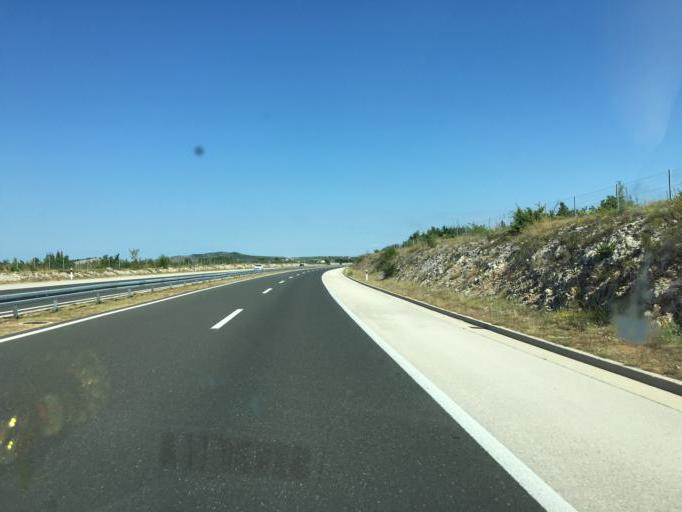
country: HR
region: Zadarska
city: Polaca
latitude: 44.0424
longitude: 15.5517
